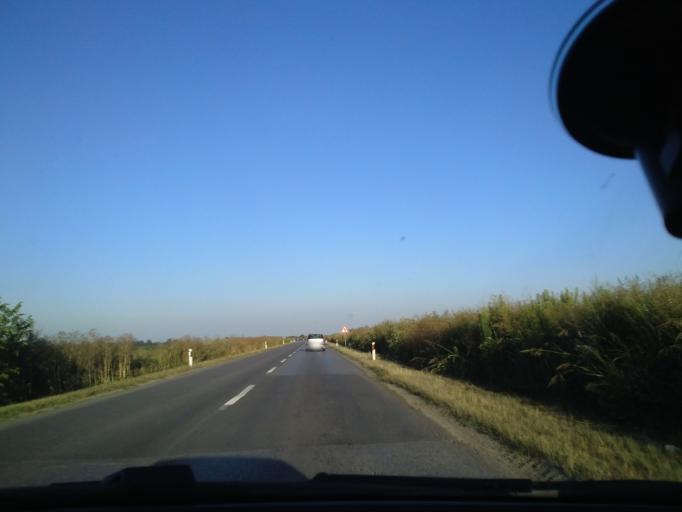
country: RS
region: Autonomna Pokrajina Vojvodina
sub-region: Juznobacki Okrug
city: Backi Petrovac
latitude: 45.3453
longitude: 19.6329
